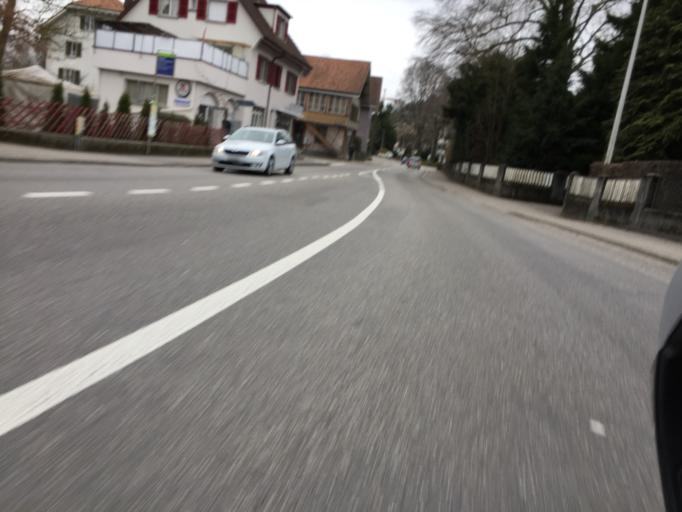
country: CH
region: Bern
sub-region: Emmental District
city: Burgdorf
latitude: 47.0545
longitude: 7.6248
